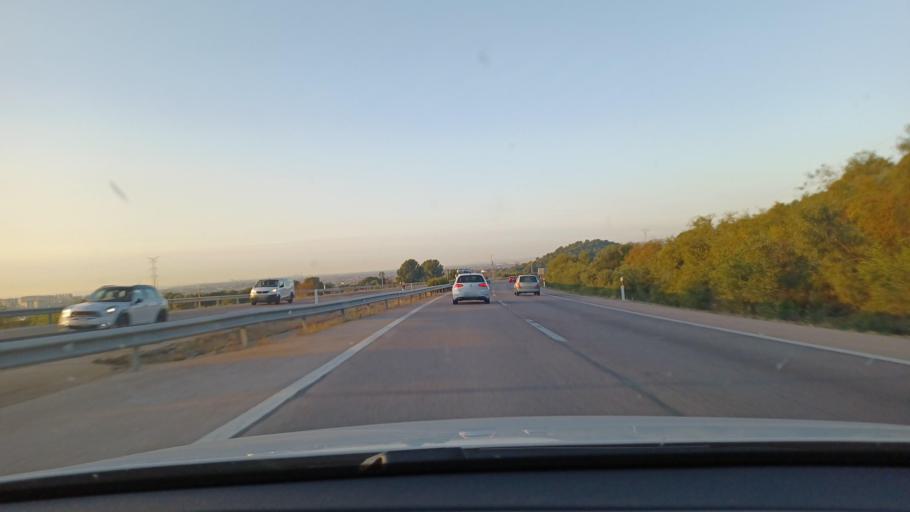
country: ES
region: Valencia
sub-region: Provincia de Castello
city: Benicassim
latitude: 40.0516
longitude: 0.0398
